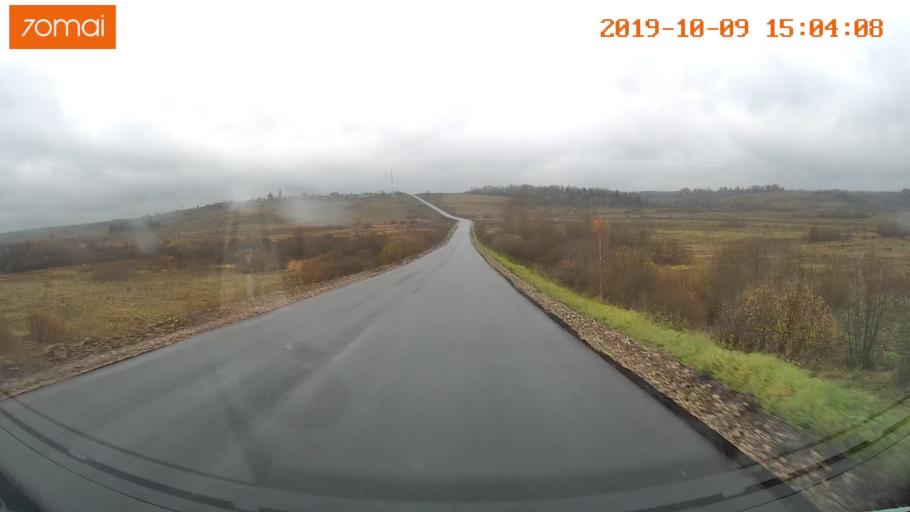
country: RU
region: Kostroma
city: Chistyye Bory
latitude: 58.2623
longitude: 41.6700
